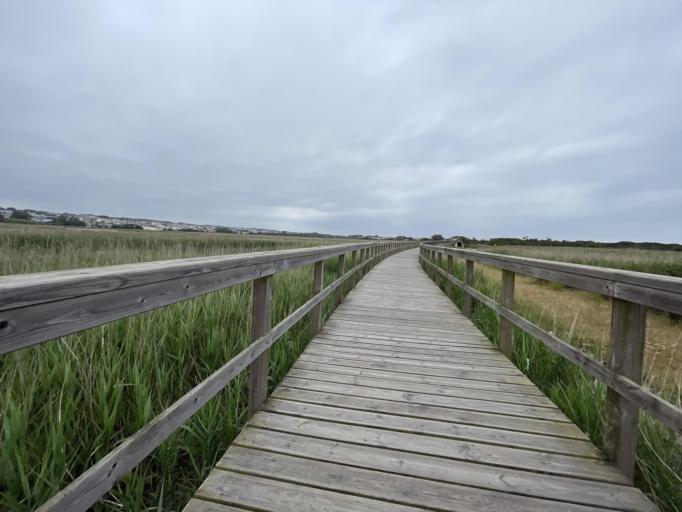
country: PT
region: Aveiro
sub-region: Ovar
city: Esmoriz
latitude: 40.9673
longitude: -8.6471
